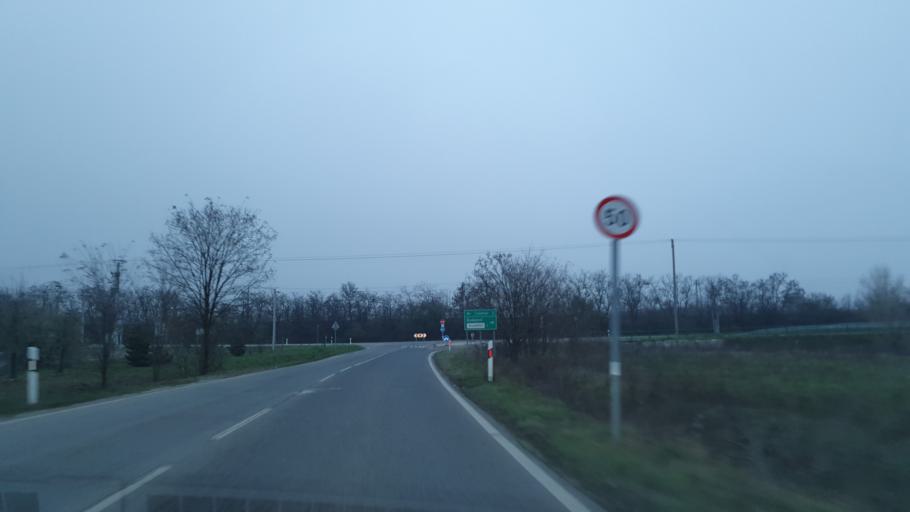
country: HU
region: Pest
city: Csomor
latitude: 47.5425
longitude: 19.2117
